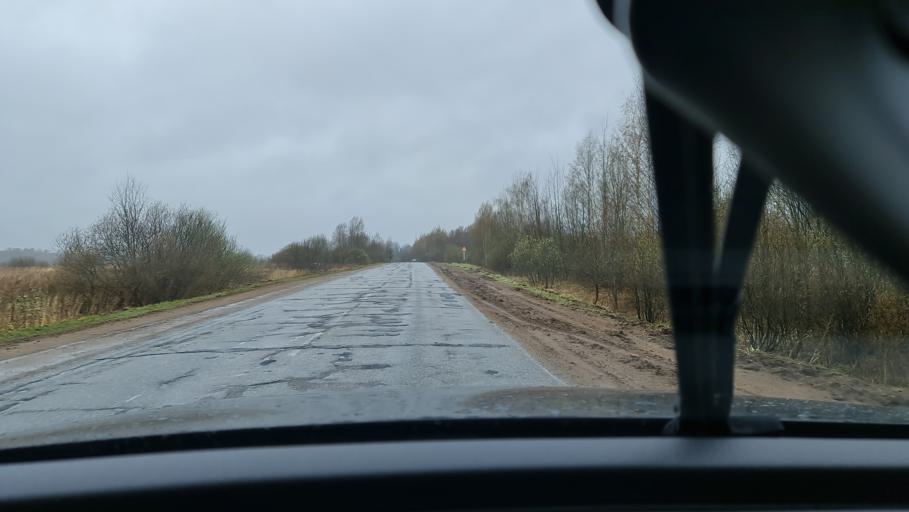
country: RU
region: Novgorod
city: Kresttsy
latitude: 58.0081
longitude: 32.7716
